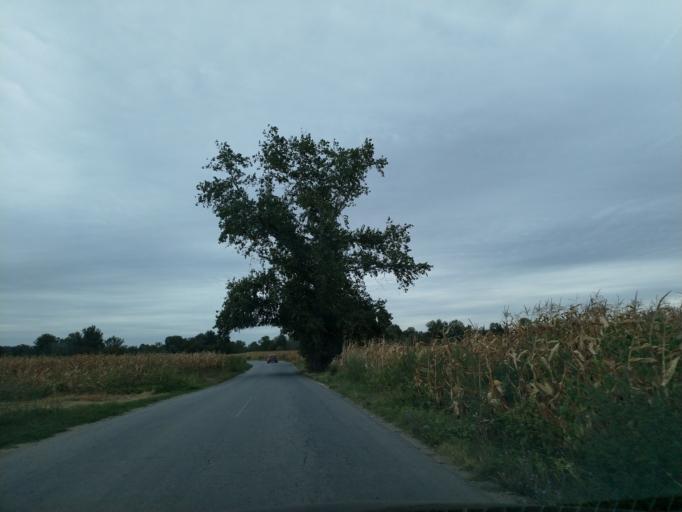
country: RS
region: Central Serbia
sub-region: Pomoravski Okrug
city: Paracin
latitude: 43.8301
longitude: 21.3373
